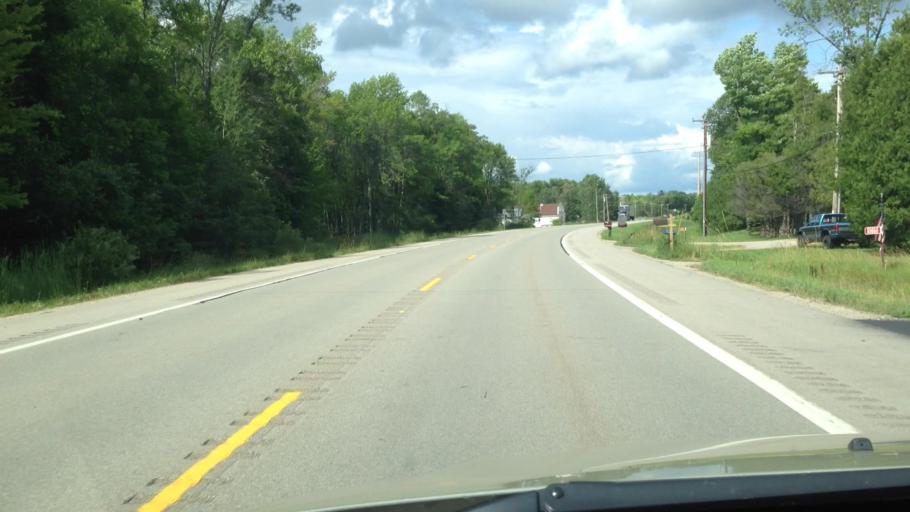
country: US
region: Michigan
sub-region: Menominee County
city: Menominee
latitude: 45.1791
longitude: -87.5693
